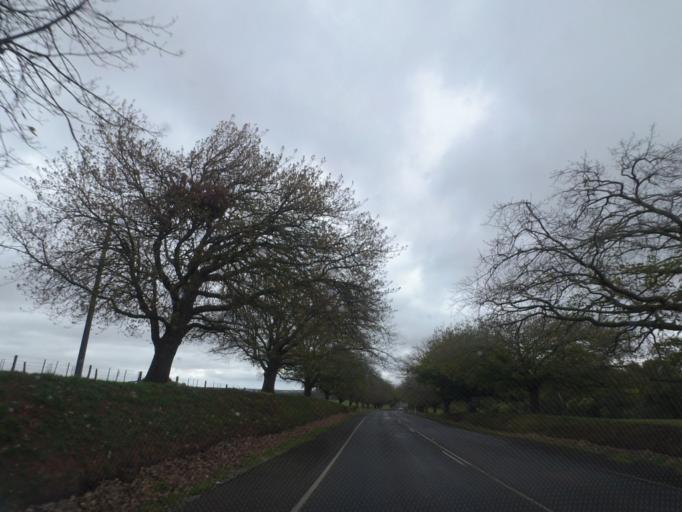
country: AU
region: Victoria
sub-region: Hume
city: Sunbury
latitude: -37.3412
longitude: 144.5287
